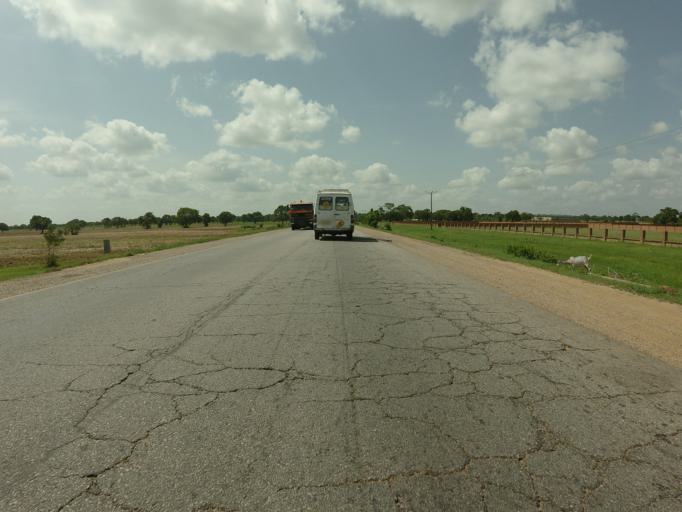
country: GH
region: Northern
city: Savelugu
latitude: 9.5670
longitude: -0.8357
